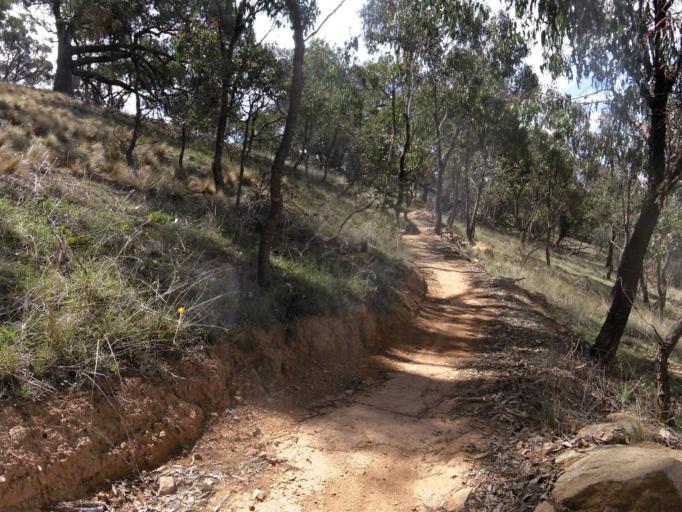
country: AU
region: Australian Capital Territory
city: Belconnen
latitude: -35.1396
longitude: 149.0938
